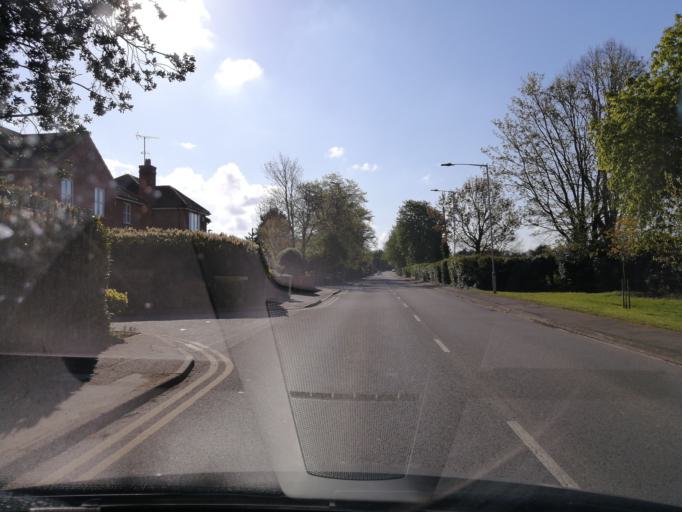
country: GB
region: England
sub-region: Peterborough
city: Peterborough
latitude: 52.6038
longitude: -0.2547
